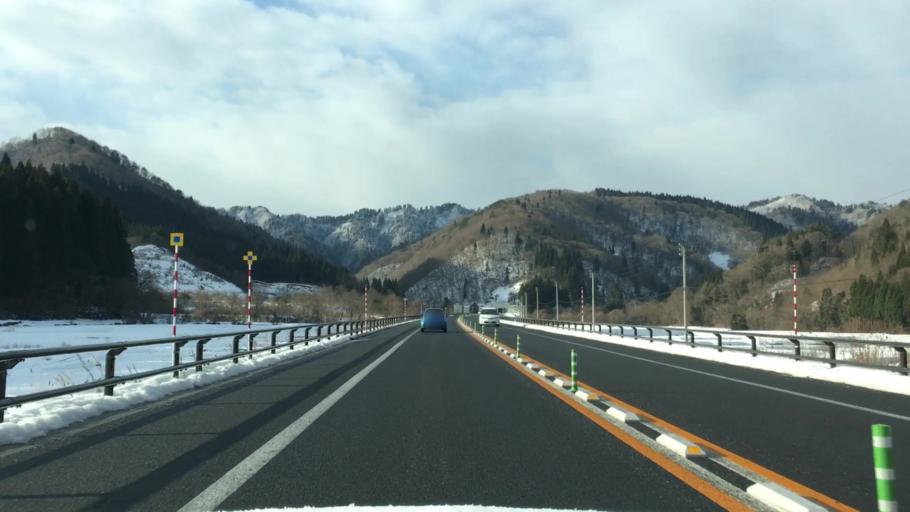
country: JP
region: Akita
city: Odate
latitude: 40.2338
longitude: 140.4961
